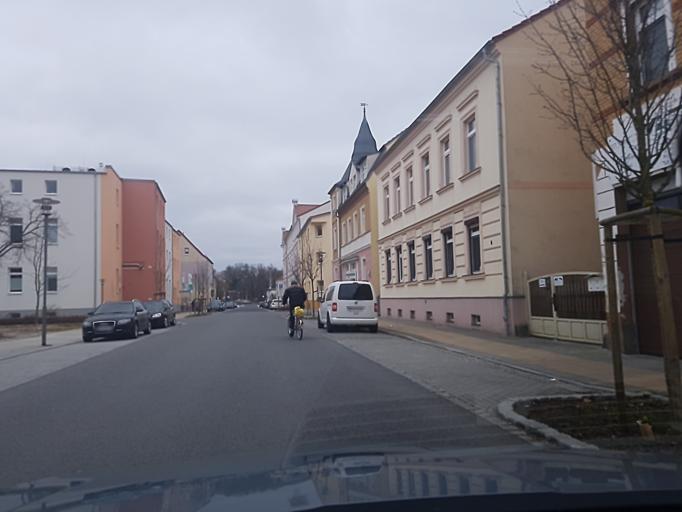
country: DE
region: Brandenburg
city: Elsterwerda
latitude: 51.4570
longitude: 13.5205
